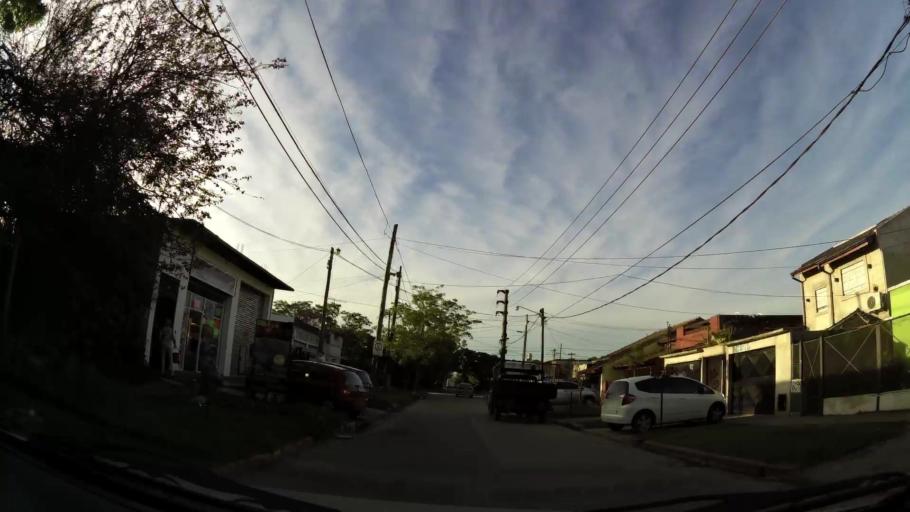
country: AR
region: Buenos Aires
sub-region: Partido de Almirante Brown
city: Adrogue
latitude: -34.7967
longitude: -58.3565
